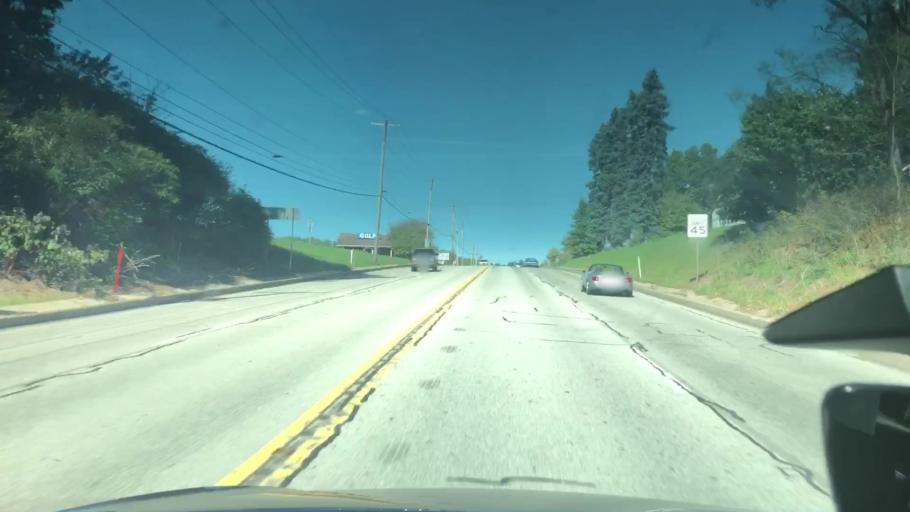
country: US
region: Pennsylvania
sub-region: Allegheny County
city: Bakerstown
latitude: 40.6533
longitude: -79.9359
